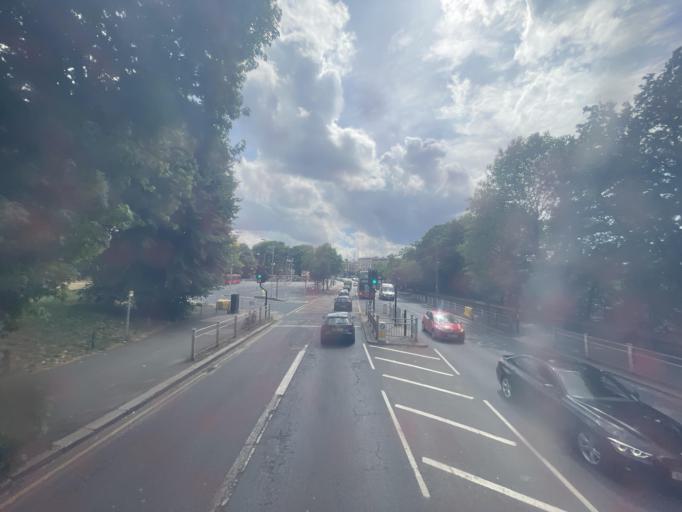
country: GB
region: England
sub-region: Greater London
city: Thornton Heath
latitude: 51.4215
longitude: -0.0776
